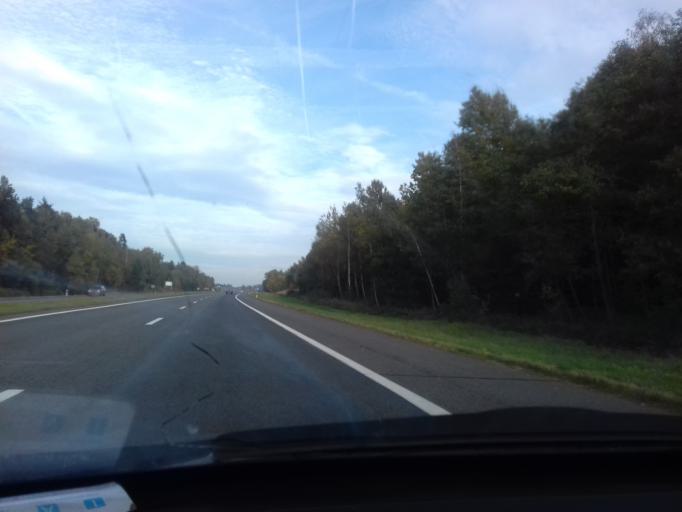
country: BY
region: Minsk
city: Hatava
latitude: 53.7541
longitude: 27.6517
